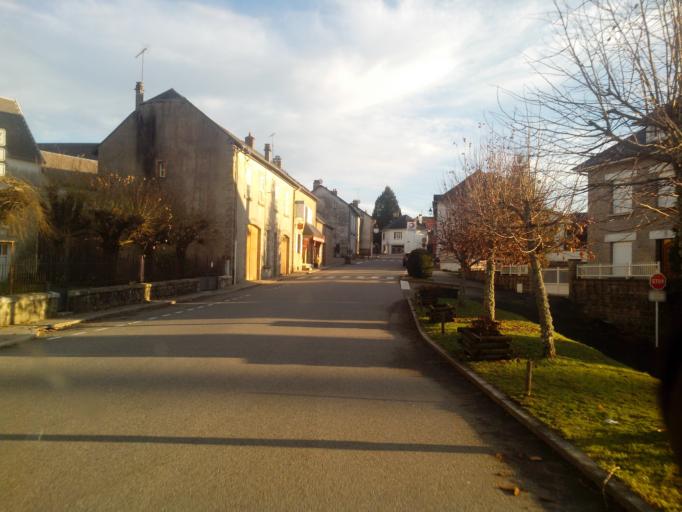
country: FR
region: Limousin
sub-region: Departement de la Correze
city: Bugeat
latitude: 45.5996
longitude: 1.9246
